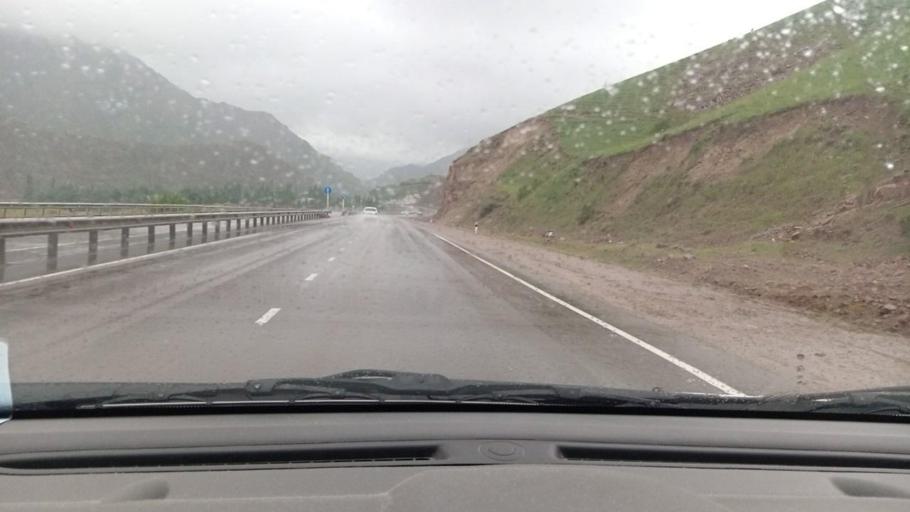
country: UZ
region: Toshkent
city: Angren
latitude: 41.1125
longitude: 70.3385
